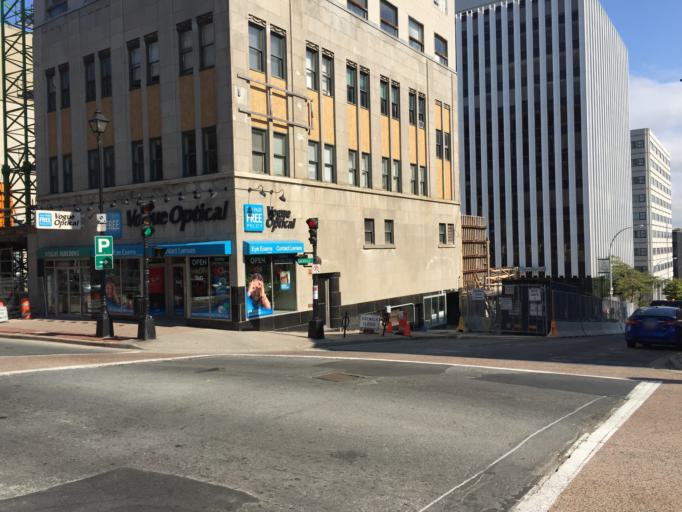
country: CA
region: Nova Scotia
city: Halifax
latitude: 44.6462
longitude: -63.5736
